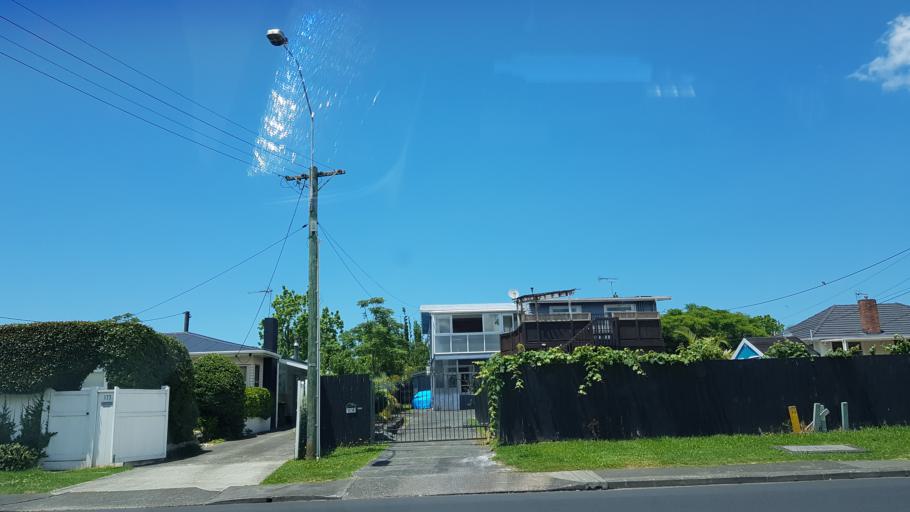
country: NZ
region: Auckland
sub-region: Auckland
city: North Shore
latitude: -36.7899
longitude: 174.6923
